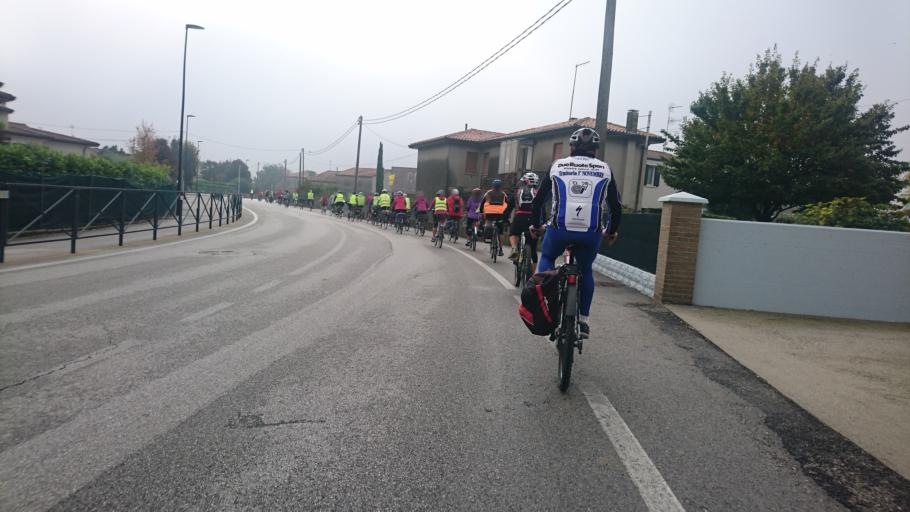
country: IT
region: Veneto
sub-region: Provincia di Padova
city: Pozzonovo
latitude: 45.1910
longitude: 11.7895
